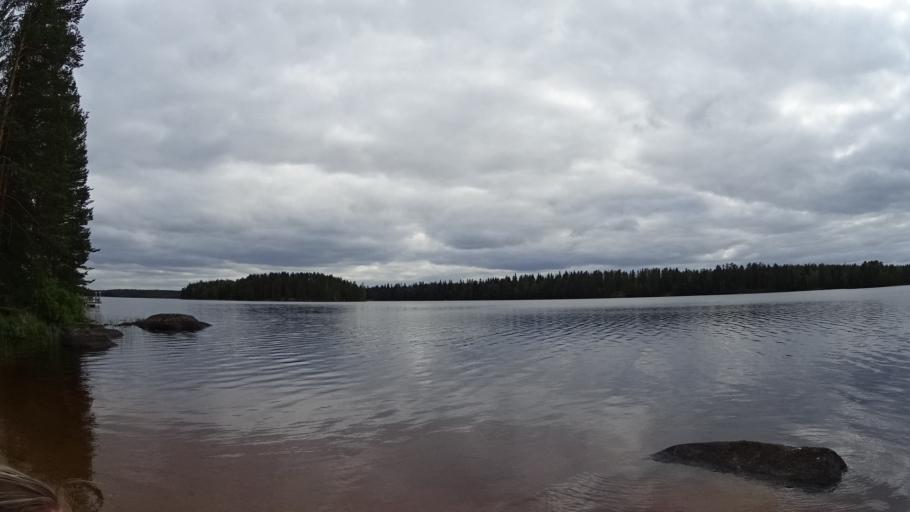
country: FI
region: Southern Ostrobothnia
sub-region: Kuusiokunnat
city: AEhtaeri
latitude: 62.5309
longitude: 24.1877
